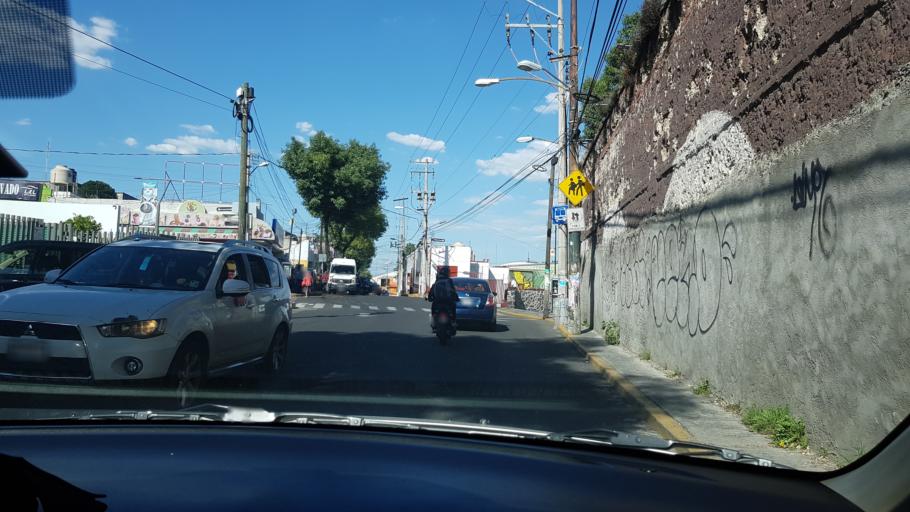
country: MX
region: Mexico City
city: Magdalena Contreras
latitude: 19.3050
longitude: -99.2355
